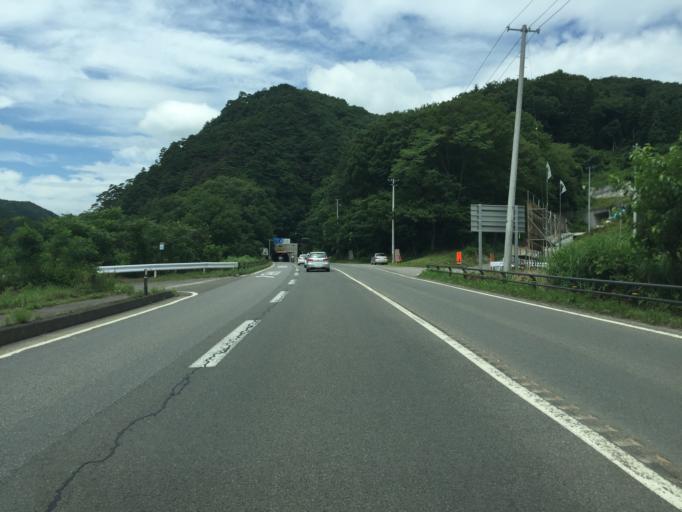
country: JP
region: Fukushima
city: Fukushima-shi
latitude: 37.8362
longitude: 140.3823
